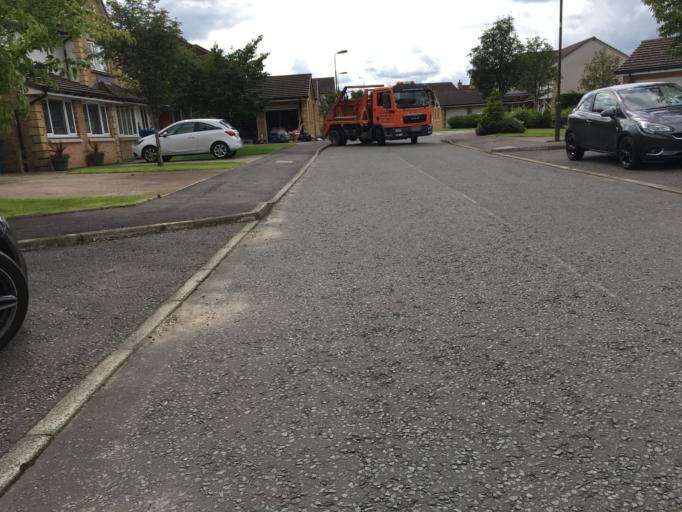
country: GB
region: Scotland
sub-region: West Lothian
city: Livingston
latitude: 55.8706
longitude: -3.5120
